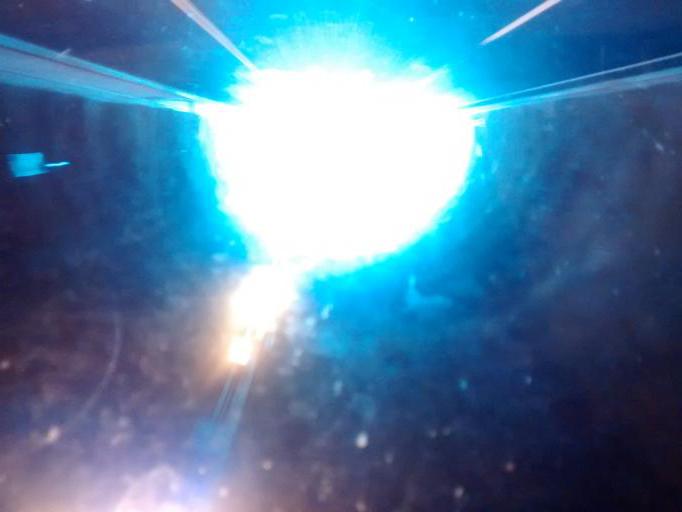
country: ES
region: Catalonia
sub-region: Provincia de Barcelona
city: Sant Pere de Ribes
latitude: 41.3012
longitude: 1.7258
